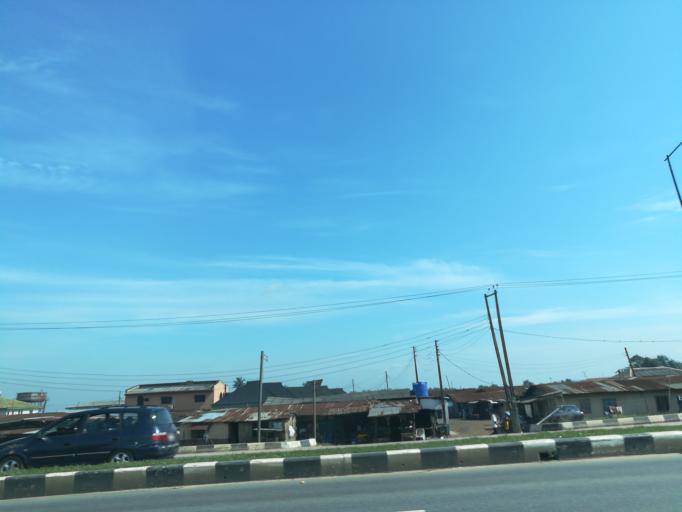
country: NG
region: Lagos
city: Ebute Ikorodu
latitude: 6.6186
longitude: 3.4676
